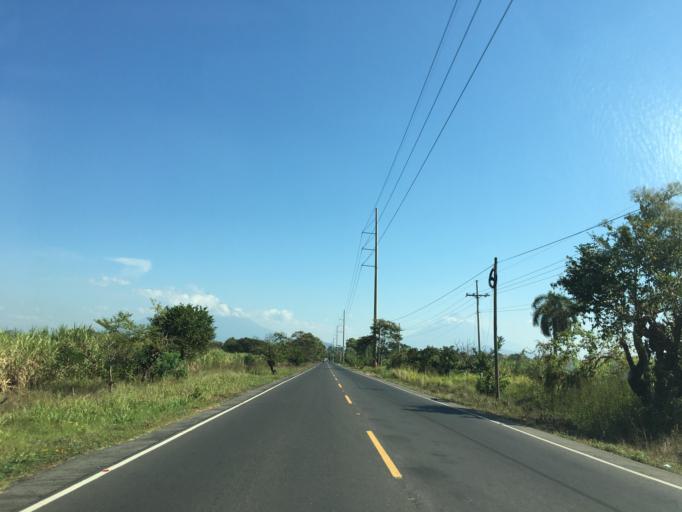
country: GT
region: Escuintla
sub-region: Municipio de La Democracia
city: La Democracia
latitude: 14.2142
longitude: -90.9552
